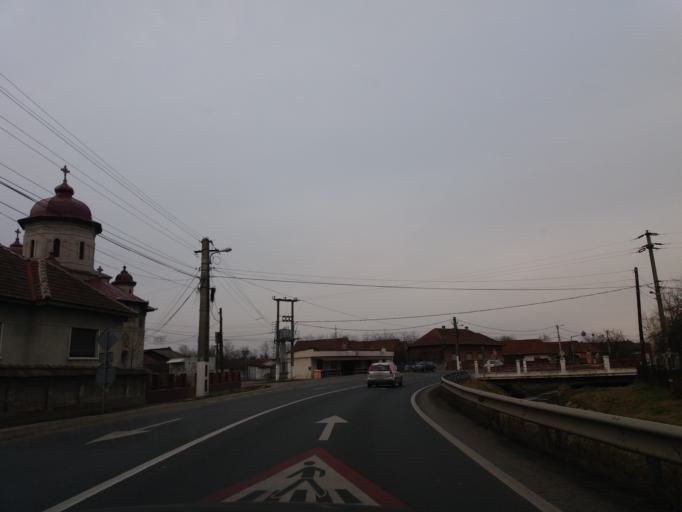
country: RO
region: Hunedoara
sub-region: Comuna Bacia
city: Bacia
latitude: 45.7773
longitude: 23.0006
